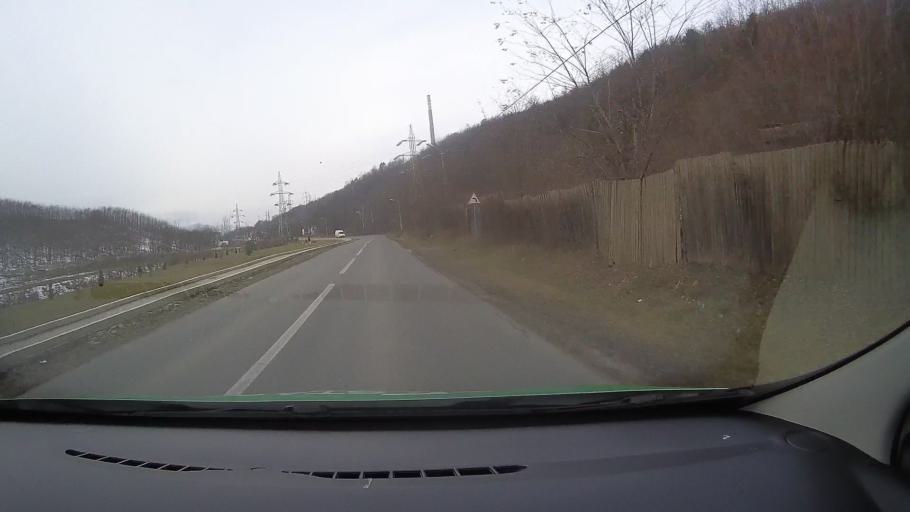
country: RO
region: Alba
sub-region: Oras Zlatna
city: Zlatna
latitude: 46.1037
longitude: 23.2457
